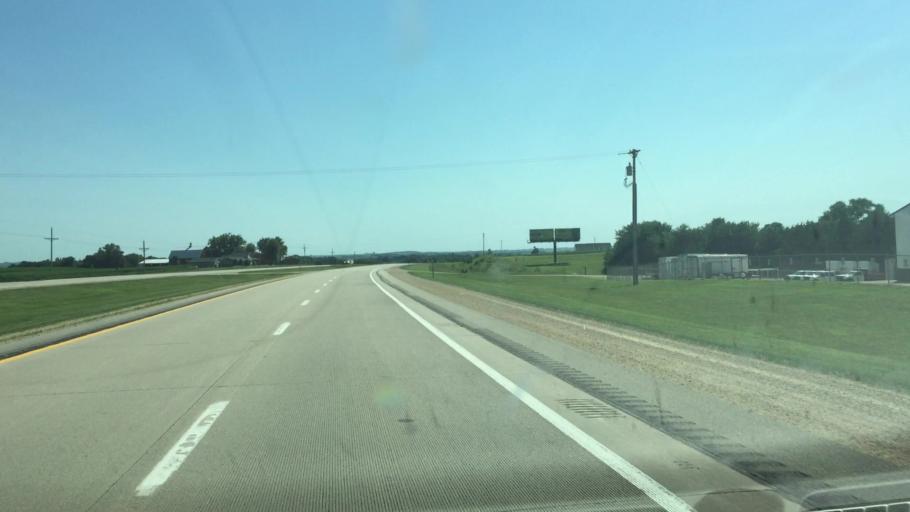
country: US
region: Iowa
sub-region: Jones County
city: Monticello
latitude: 42.2666
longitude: -91.1451
